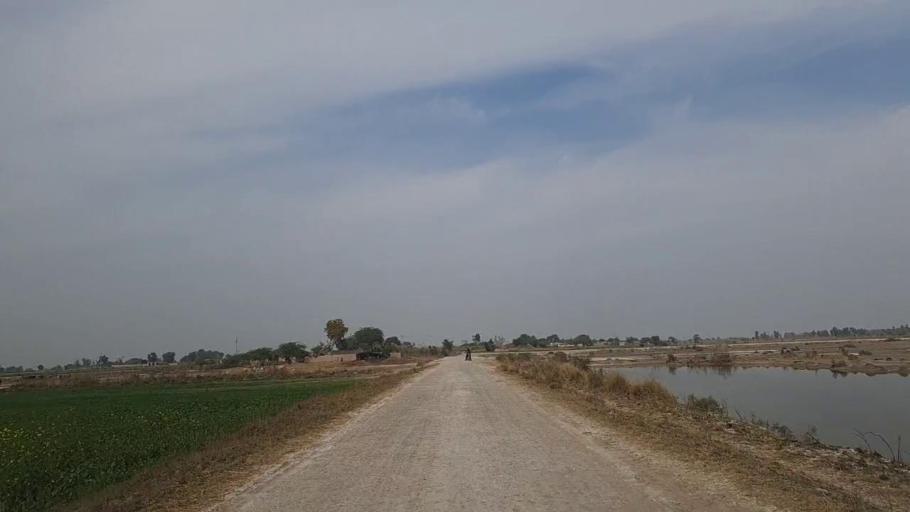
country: PK
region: Sindh
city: Daur
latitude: 26.4764
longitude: 68.4024
